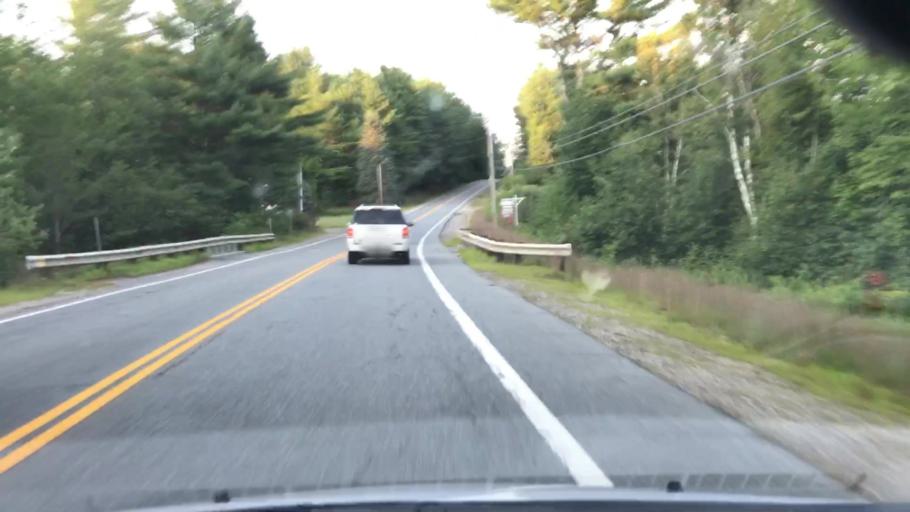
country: US
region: New Hampshire
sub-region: Grafton County
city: Rumney
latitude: 43.8800
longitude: -71.9104
